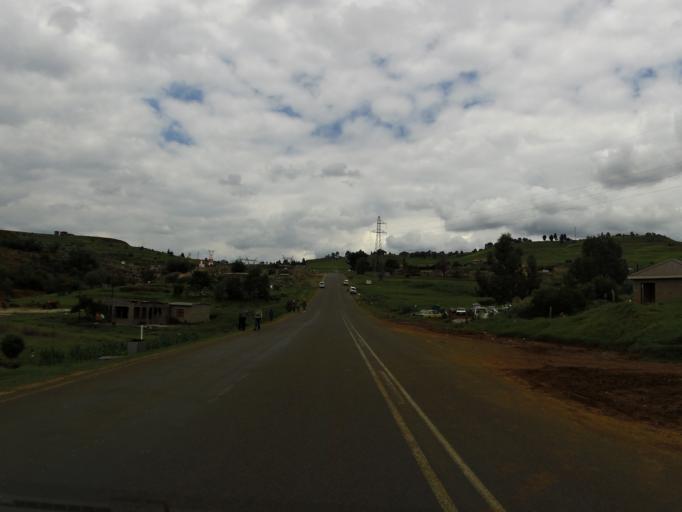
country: LS
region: Leribe
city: Leribe
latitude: -28.9927
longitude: 28.1932
